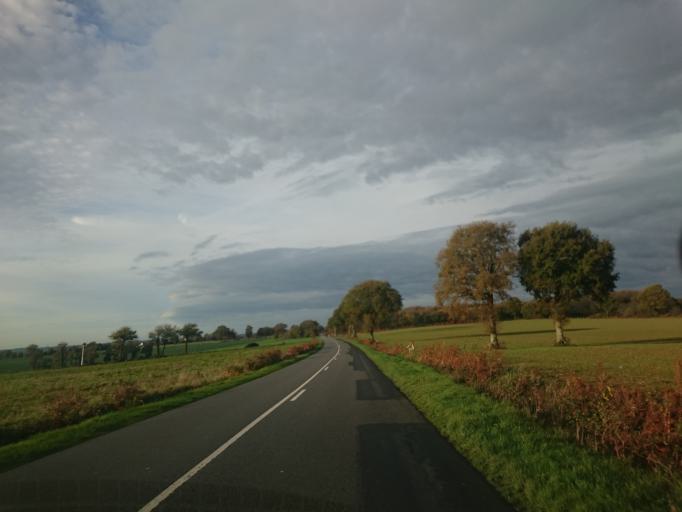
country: FR
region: Brittany
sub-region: Departement d'Ille-et-Vilaine
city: Crevin
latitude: 47.9285
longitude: -1.6820
